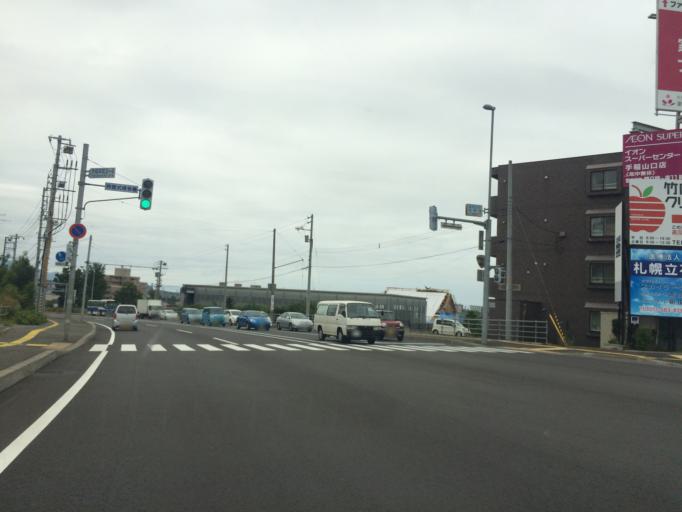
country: JP
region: Hokkaido
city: Sapporo
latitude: 43.1210
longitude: 141.2359
